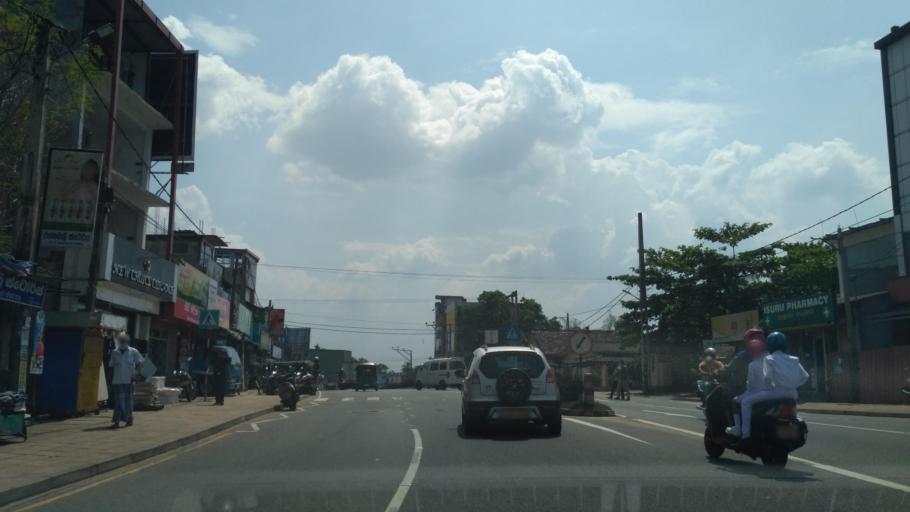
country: LK
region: North Western
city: Kurunegala
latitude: 7.4306
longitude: 80.2144
